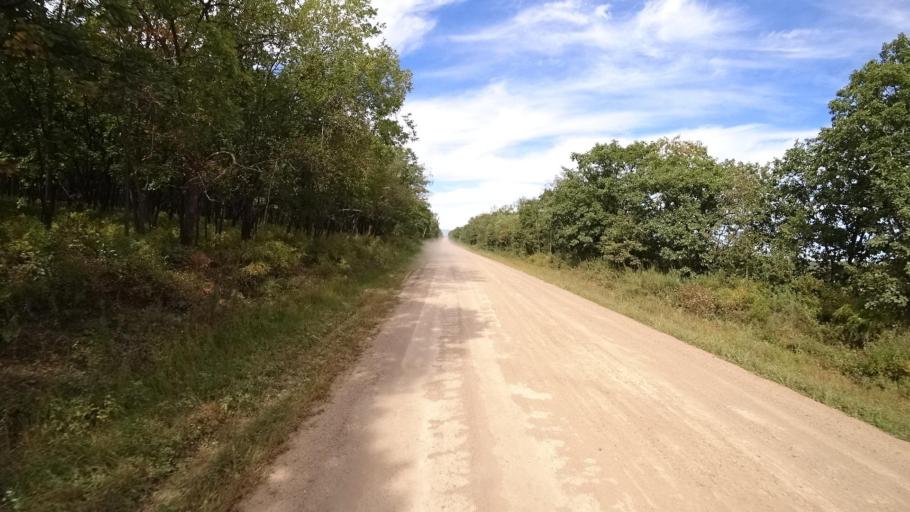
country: RU
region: Primorskiy
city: Yakovlevka
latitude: 44.5985
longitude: 133.6056
